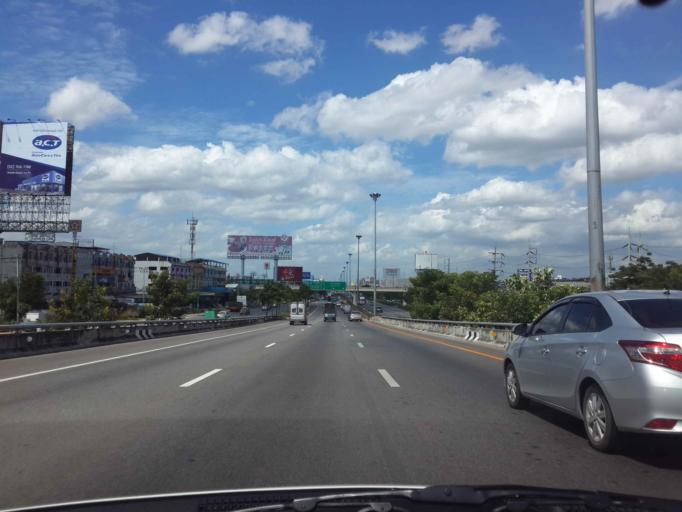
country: TH
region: Bangkok
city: Bang Bon
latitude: 13.6435
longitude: 100.4119
